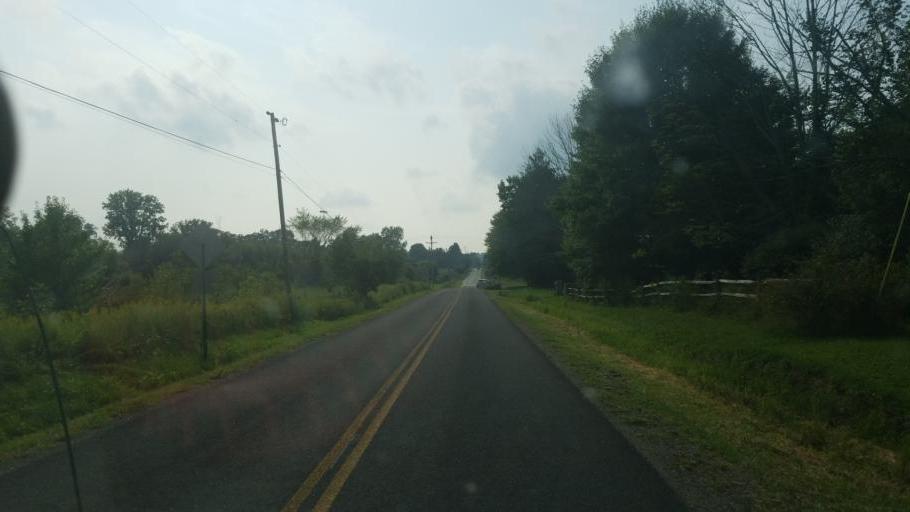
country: US
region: Ohio
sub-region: Medina County
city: Westfield Center
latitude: 41.0512
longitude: -81.8958
